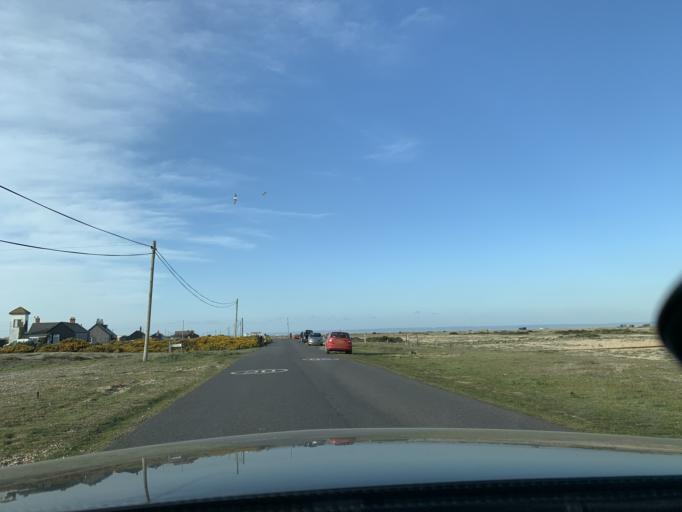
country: GB
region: England
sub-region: Kent
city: New Romney
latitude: 50.9195
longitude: 0.9767
